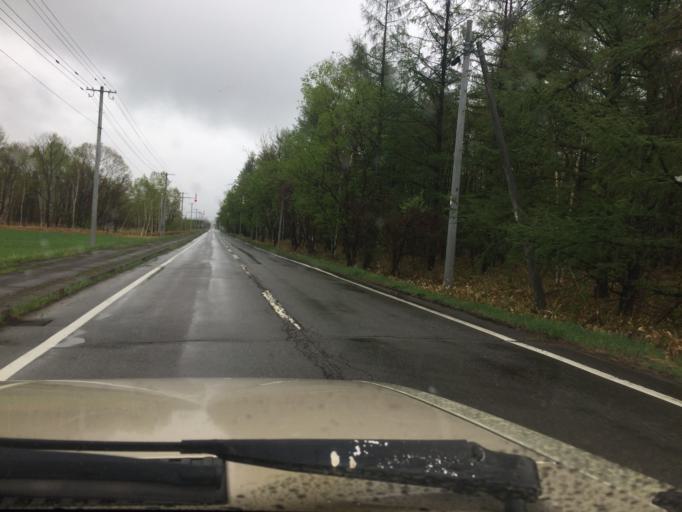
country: JP
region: Hokkaido
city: Obihiro
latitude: 42.8086
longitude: 142.9627
